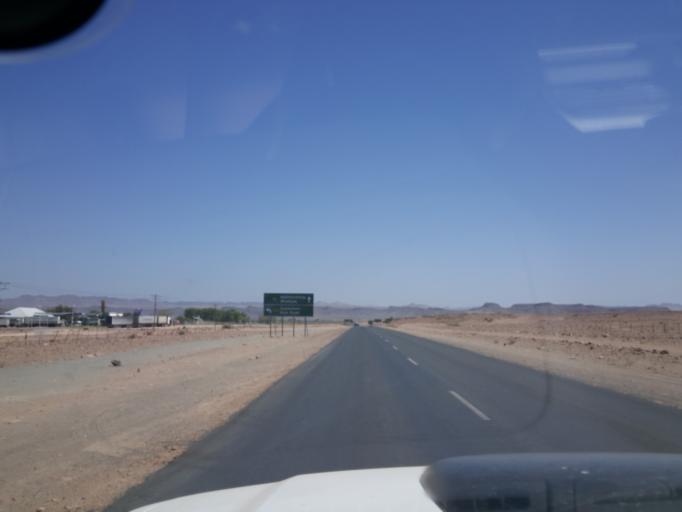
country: ZA
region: Northern Cape
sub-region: Namakwa District Municipality
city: Port Nolloth
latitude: -28.7395
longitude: 17.6175
